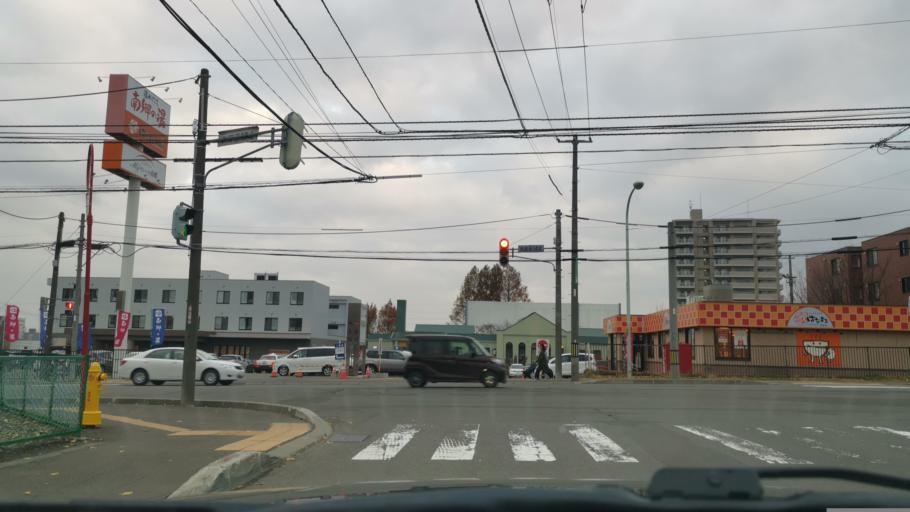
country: JP
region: Hokkaido
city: Sapporo
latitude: 43.0369
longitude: 141.4236
